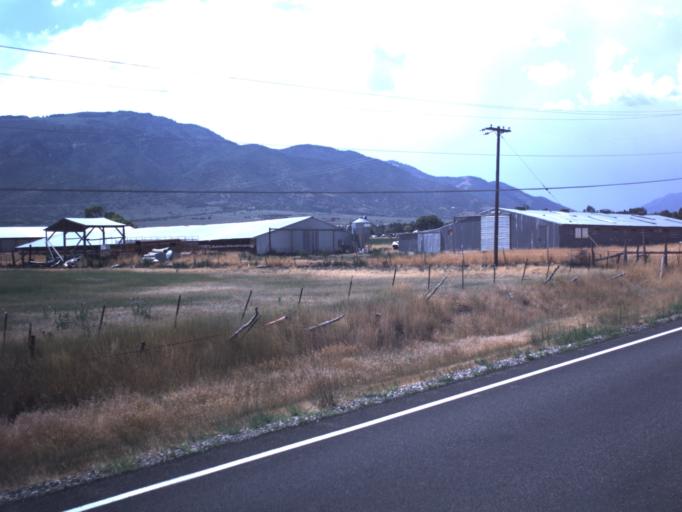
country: US
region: Utah
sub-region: Sanpete County
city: Fountain Green
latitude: 39.6166
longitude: -111.6296
